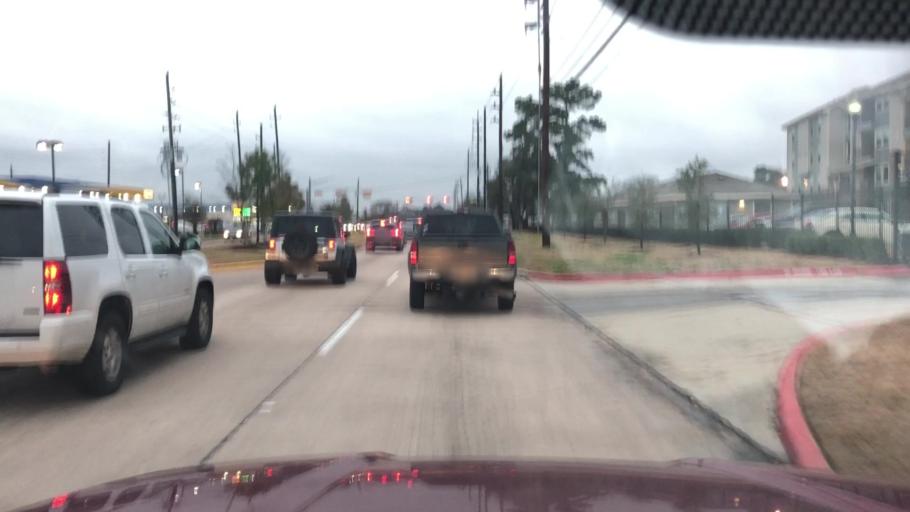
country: US
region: Texas
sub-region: Harris County
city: Tomball
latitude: 30.0445
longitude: -95.5382
